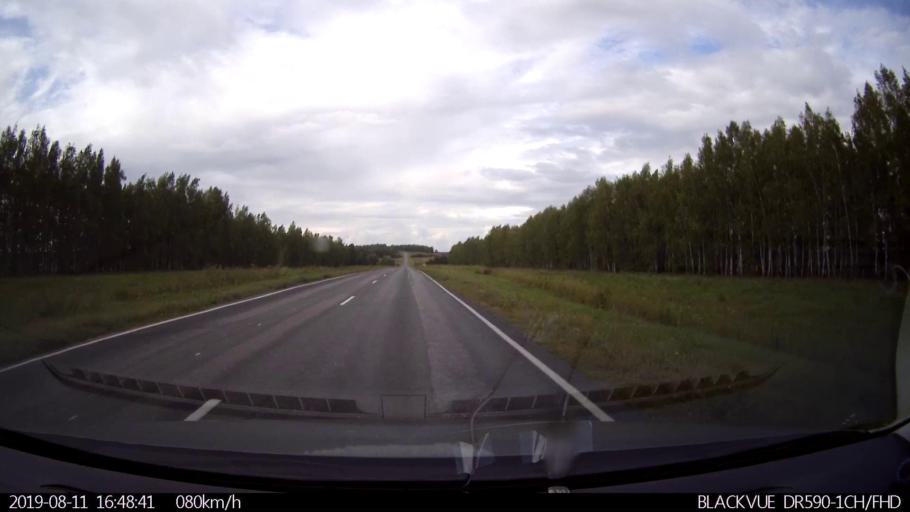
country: RU
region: Ulyanovsk
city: Mayna
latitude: 54.2115
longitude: 47.6930
